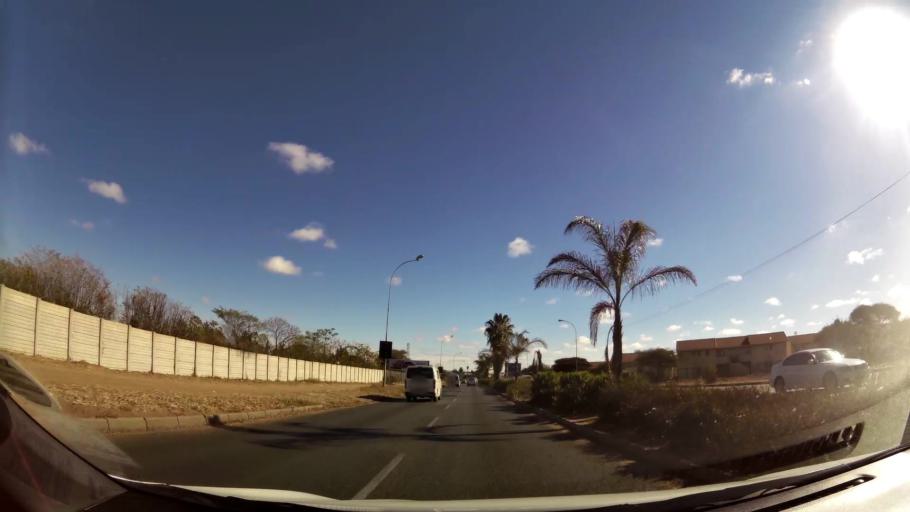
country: ZA
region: Limpopo
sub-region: Capricorn District Municipality
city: Polokwane
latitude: -23.8845
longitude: 29.4438
